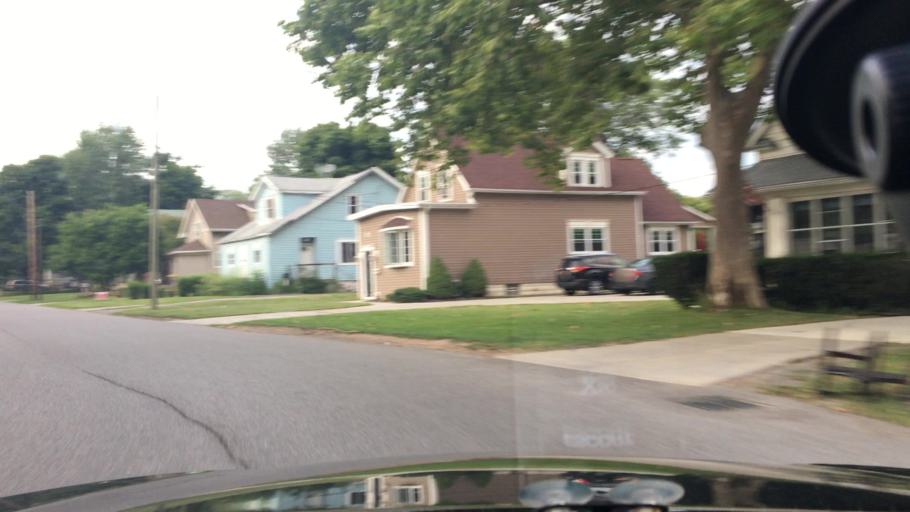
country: US
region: New York
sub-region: Erie County
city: West Seneca
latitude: 42.8371
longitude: -78.7746
